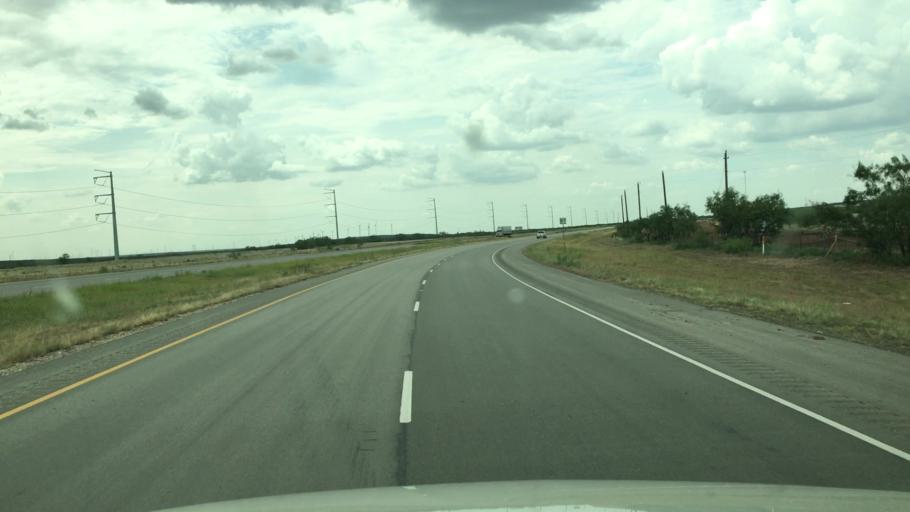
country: US
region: Texas
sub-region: Glasscock County
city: Garden City
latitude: 31.9687
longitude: -101.2386
